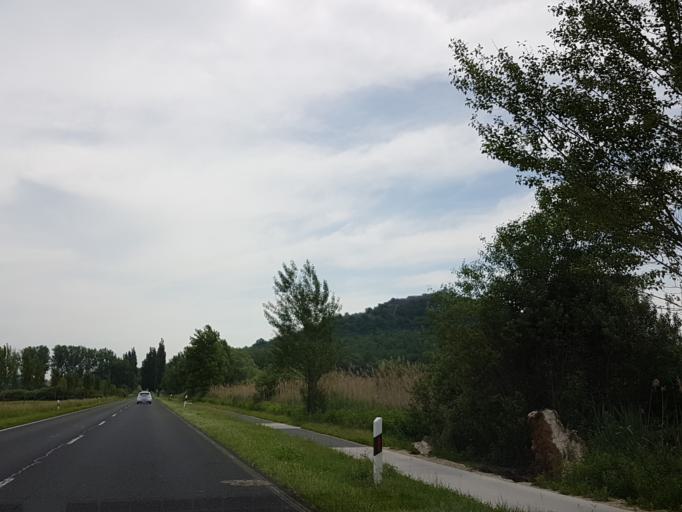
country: HU
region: Veszprem
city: Tapolca
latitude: 46.8060
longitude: 17.4227
